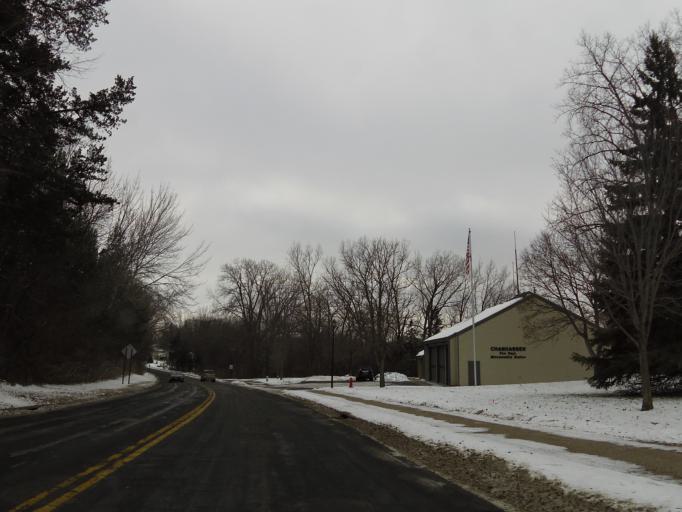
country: US
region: Minnesota
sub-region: Hennepin County
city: Shorewood
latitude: 44.8883
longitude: -93.6162
